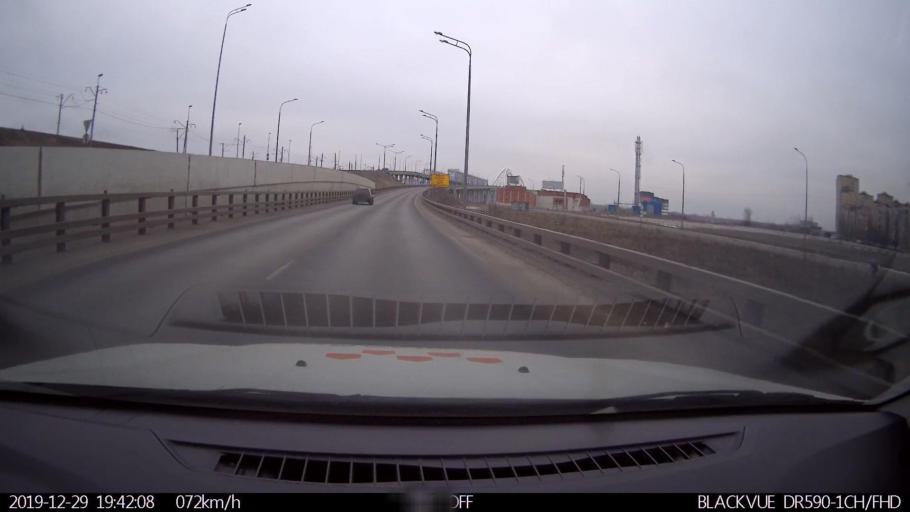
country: RU
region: Nizjnij Novgorod
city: Nizhniy Novgorod
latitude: 56.3468
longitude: 43.9220
